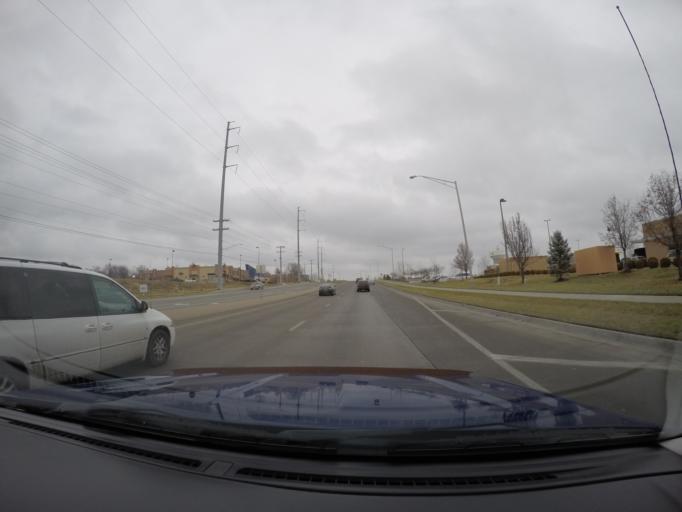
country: US
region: Kansas
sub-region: Wyandotte County
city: Edwardsville
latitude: 39.1284
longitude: -94.8247
